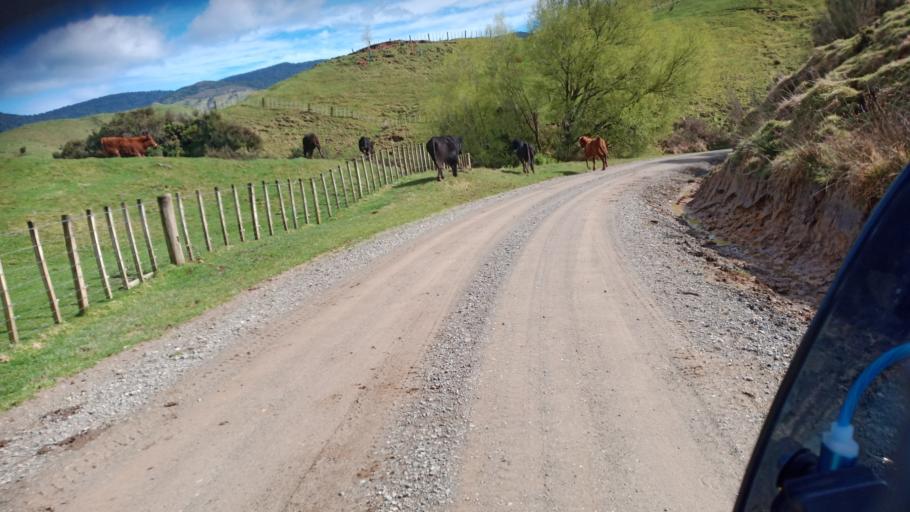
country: NZ
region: Hawke's Bay
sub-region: Wairoa District
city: Wairoa
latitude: -38.7387
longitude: 177.3118
